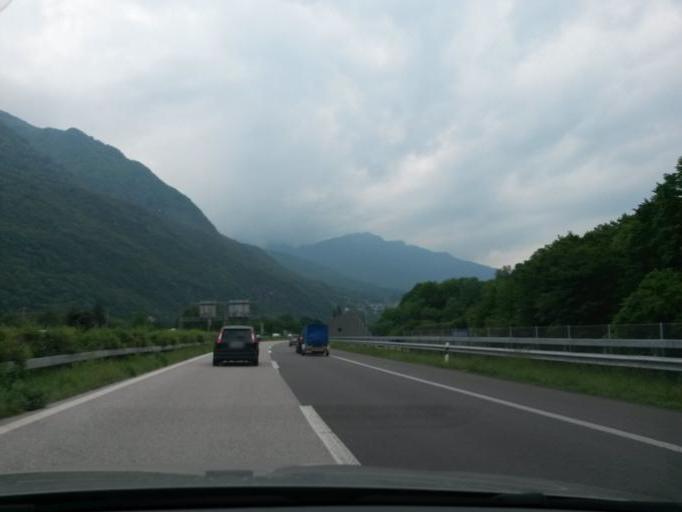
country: CH
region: Ticino
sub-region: Bellinzona District
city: Bellinzona
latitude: 46.2178
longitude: 9.0367
